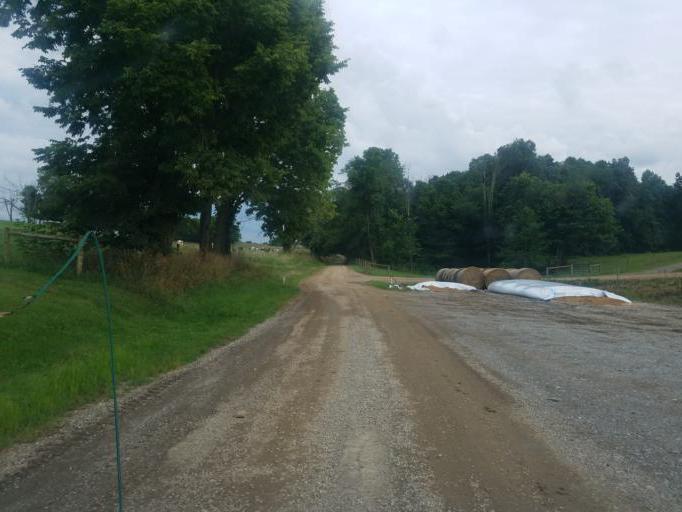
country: US
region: Ohio
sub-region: Knox County
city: Oak Hill
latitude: 40.3368
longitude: -82.1389
